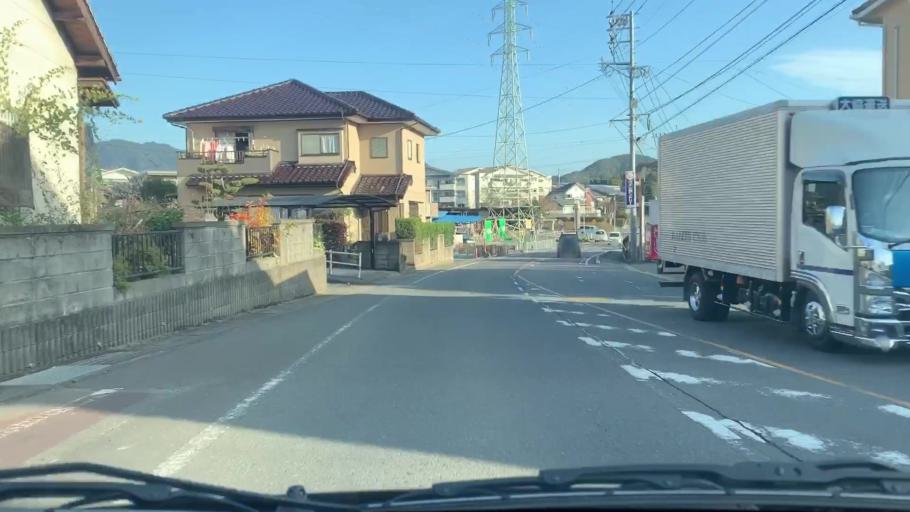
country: JP
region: Saga Prefecture
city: Takeocho-takeo
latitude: 33.2075
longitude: 130.0269
